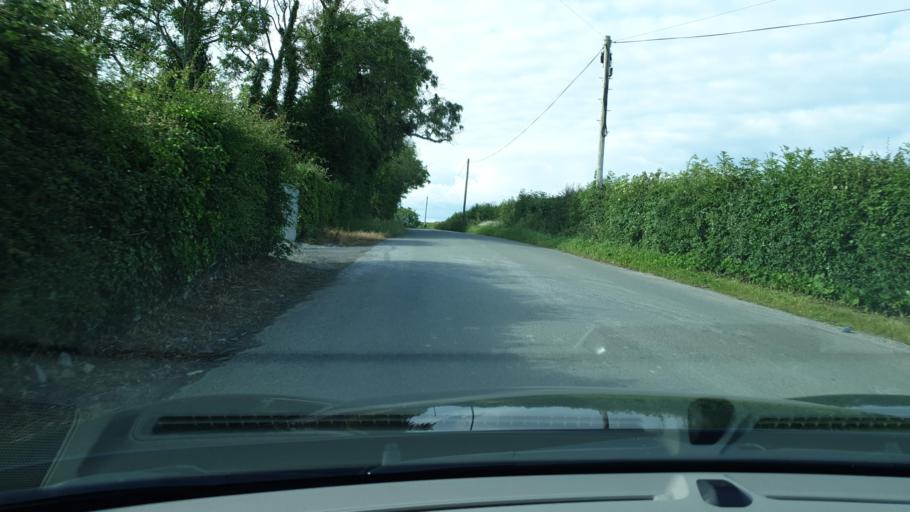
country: IE
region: Leinster
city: Balrothery
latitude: 53.5624
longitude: -6.1656
